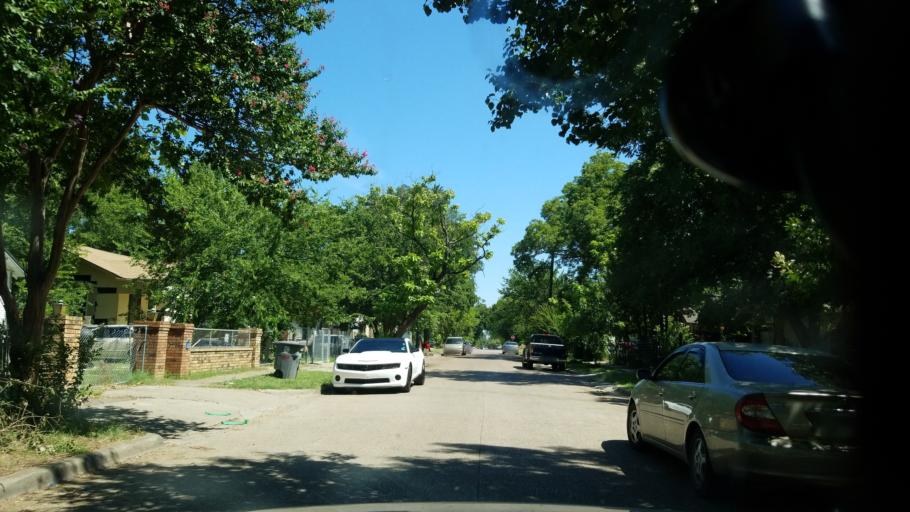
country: US
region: Texas
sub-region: Dallas County
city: Cockrell Hill
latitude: 32.7084
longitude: -96.8194
